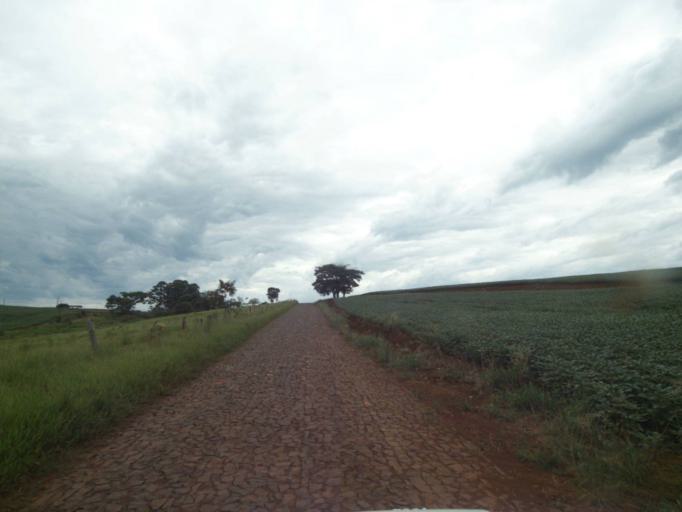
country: BR
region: Parana
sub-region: Guaraniacu
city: Guaraniacu
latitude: -24.9261
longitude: -52.9384
